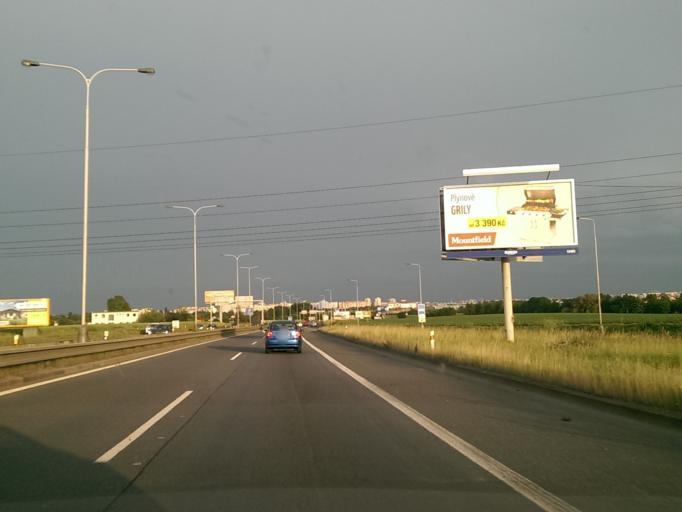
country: CZ
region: Praha
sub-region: Praha 9
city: Strizkov
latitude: 50.1558
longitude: 14.4869
